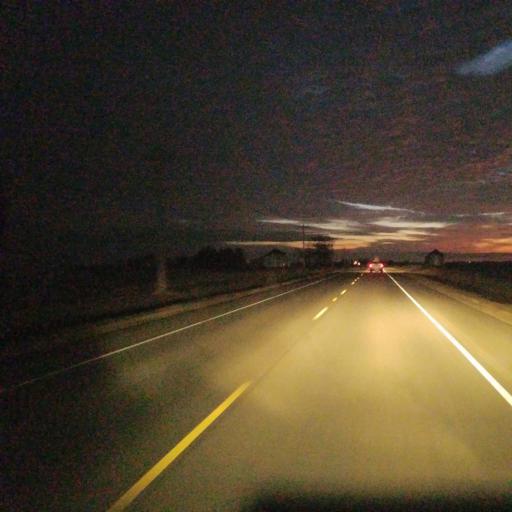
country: US
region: Illinois
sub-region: Peoria County
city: Hanna City
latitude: 40.6975
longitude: -89.8691
